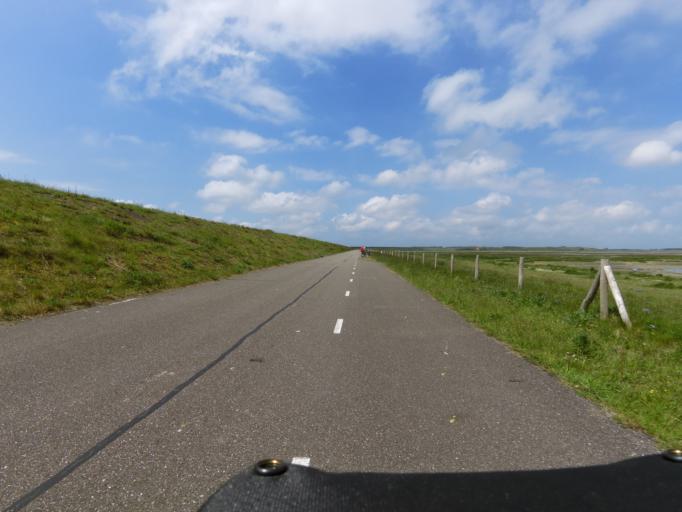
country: NL
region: Zeeland
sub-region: Schouwen-Duiveland
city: Scharendijke
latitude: 51.6841
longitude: 3.8363
